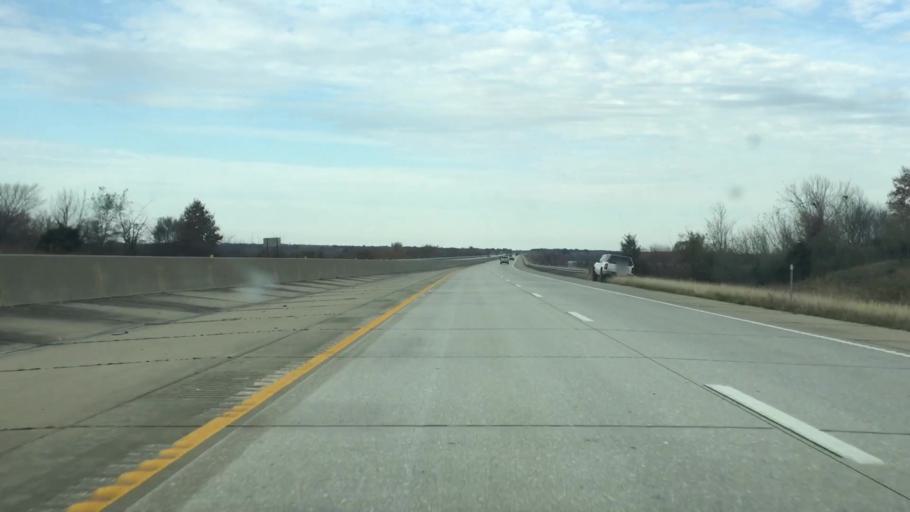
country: US
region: Missouri
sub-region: Henry County
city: Clinton
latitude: 38.3107
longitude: -93.7583
